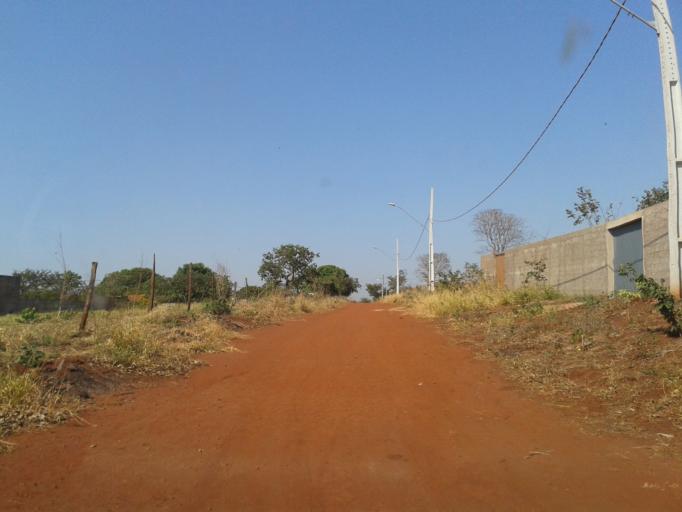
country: BR
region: Minas Gerais
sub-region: Ituiutaba
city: Ituiutaba
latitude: -18.9577
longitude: -49.4786
